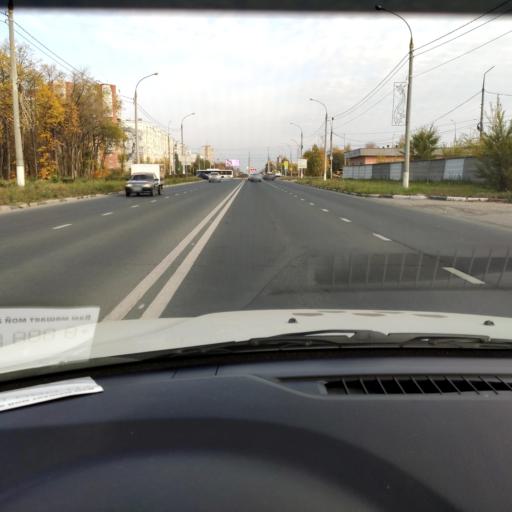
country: RU
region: Samara
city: Tol'yatti
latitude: 53.4969
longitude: 49.2894
